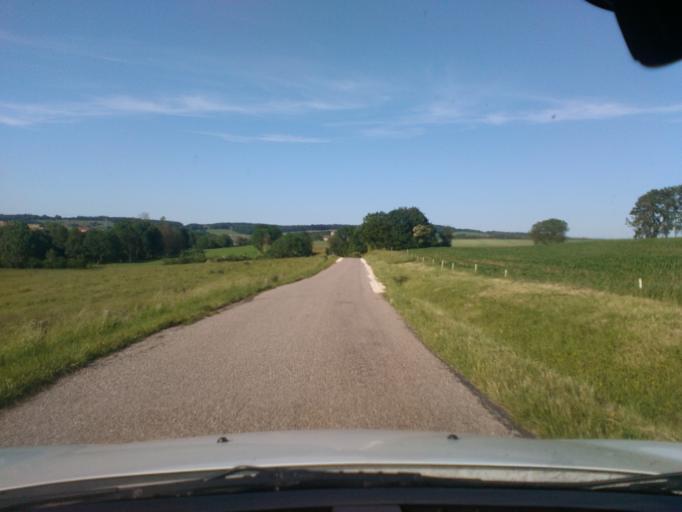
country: FR
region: Lorraine
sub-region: Departement des Vosges
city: Mirecourt
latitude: 48.2818
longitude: 6.1618
